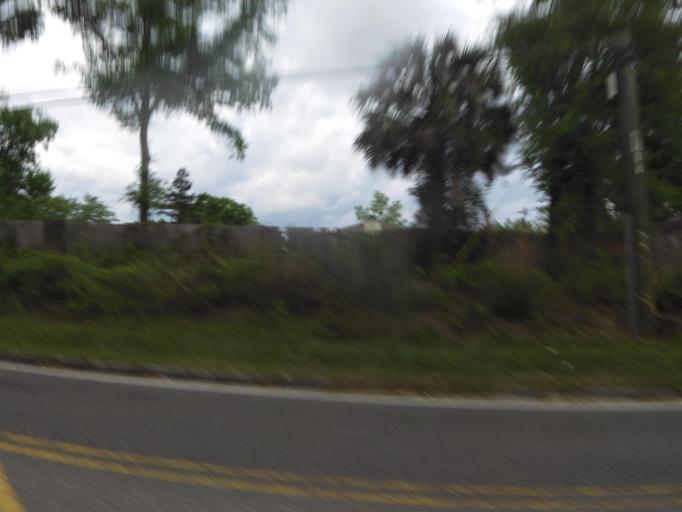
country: US
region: Florida
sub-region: Clay County
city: Bellair-Meadowbrook Terrace
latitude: 30.2007
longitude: -81.7270
